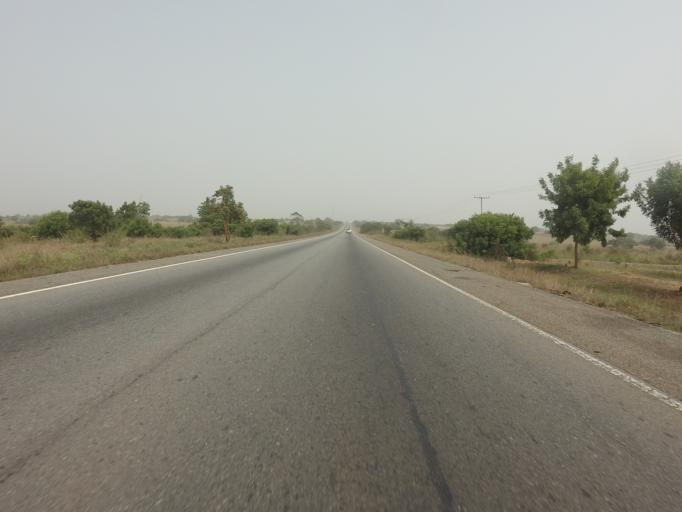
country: GH
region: Greater Accra
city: Tema
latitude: 5.8777
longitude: 0.3829
